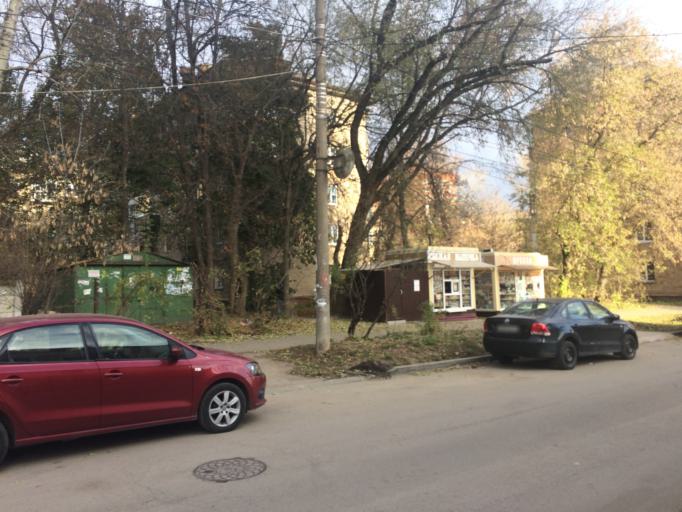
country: RU
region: Tula
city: Mendeleyevskiy
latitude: 54.1631
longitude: 37.5890
